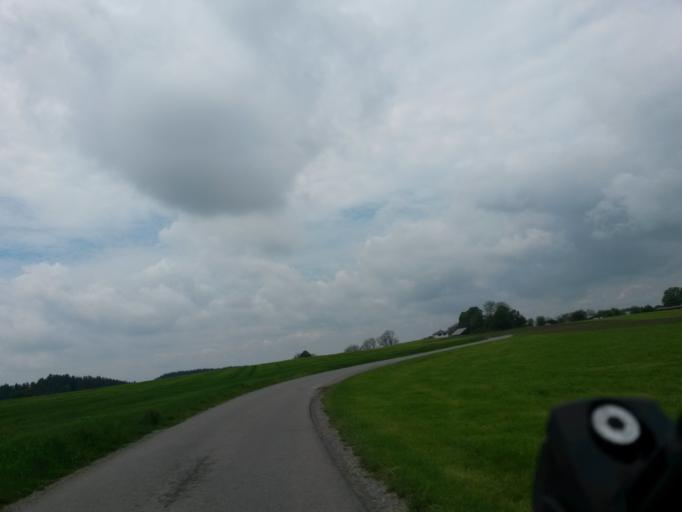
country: DE
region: Baden-Wuerttemberg
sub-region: Tuebingen Region
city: Bergatreute
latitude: 47.8680
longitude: 9.7686
